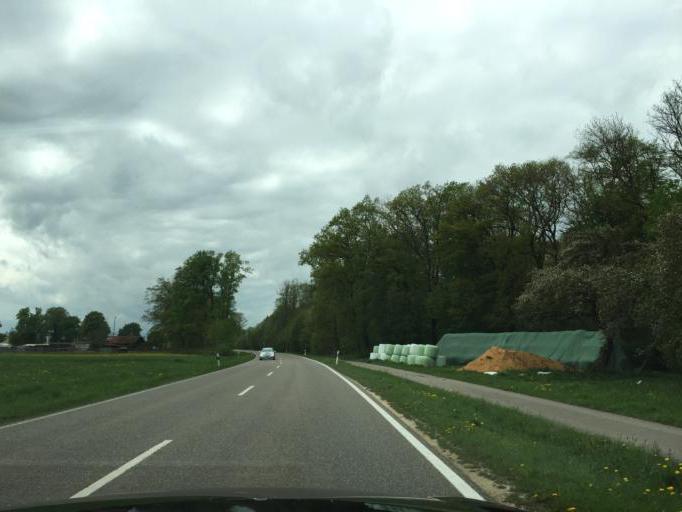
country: DE
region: Bavaria
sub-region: Swabia
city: Holzheim
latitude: 48.5596
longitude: 10.5524
